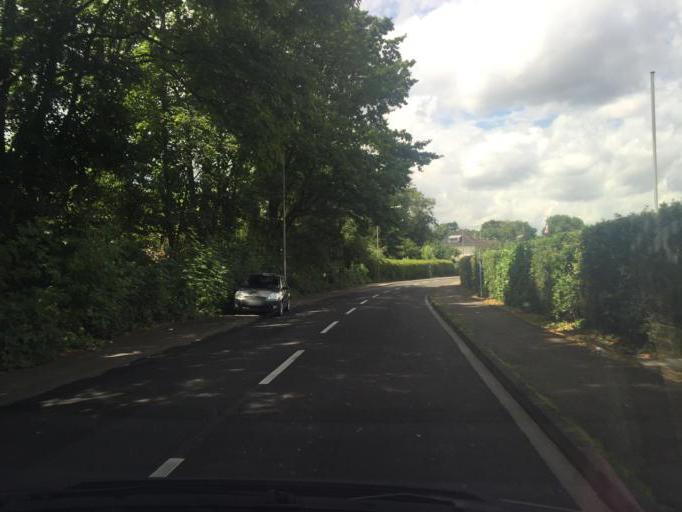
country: DE
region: North Rhine-Westphalia
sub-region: Regierungsbezirk Koln
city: Neustadt/Nord
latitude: 50.9552
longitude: 6.9463
